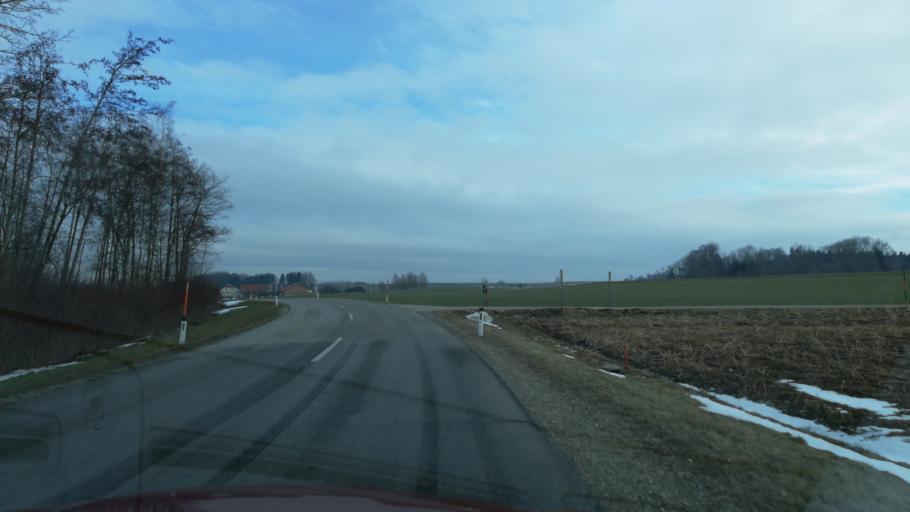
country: AT
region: Upper Austria
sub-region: Politischer Bezirk Vocklabruck
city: Wolfsegg am Hausruck
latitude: 48.1630
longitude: 13.6683
